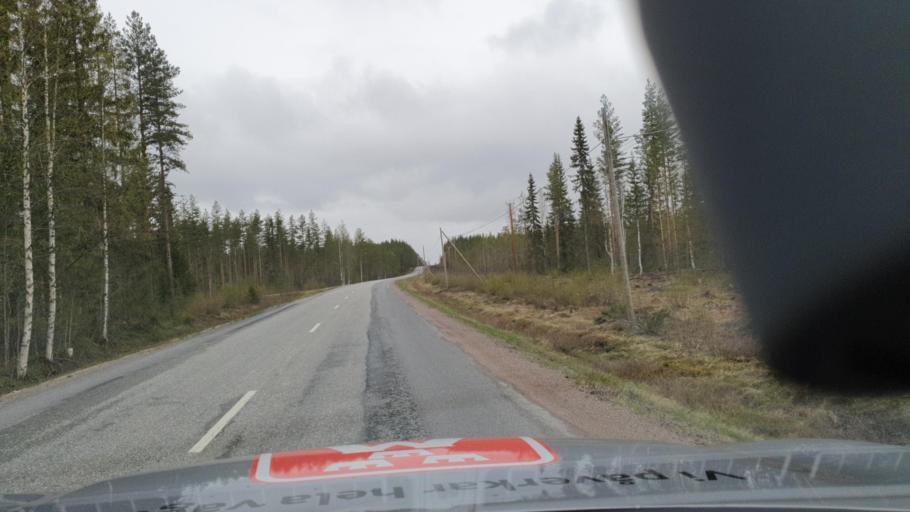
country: SE
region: Vaesternorrland
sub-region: Solleftea Kommun
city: Solleftea
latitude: 63.5955
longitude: 17.5506
